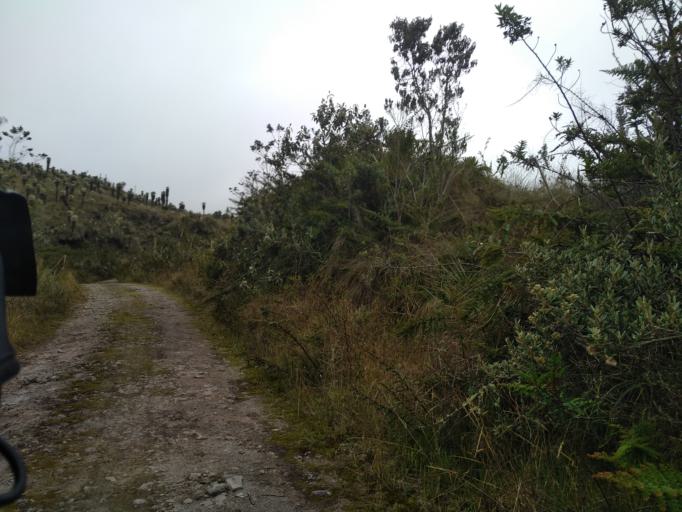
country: EC
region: Carchi
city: San Gabriel
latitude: 0.6964
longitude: -77.8444
